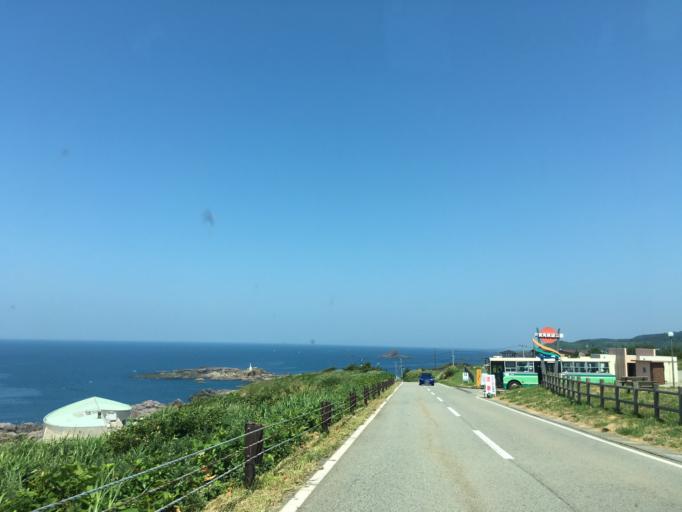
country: JP
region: Akita
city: Tenno
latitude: 39.9401
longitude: 139.7070
